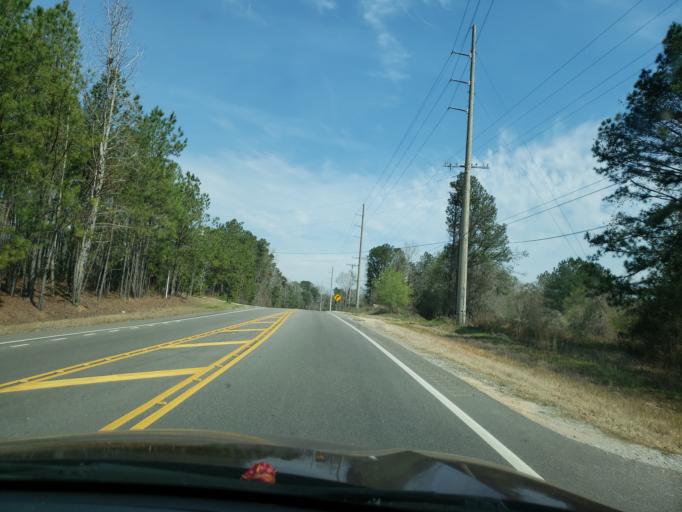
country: US
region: Alabama
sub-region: Elmore County
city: Wetumpka
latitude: 32.5540
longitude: -86.1590
